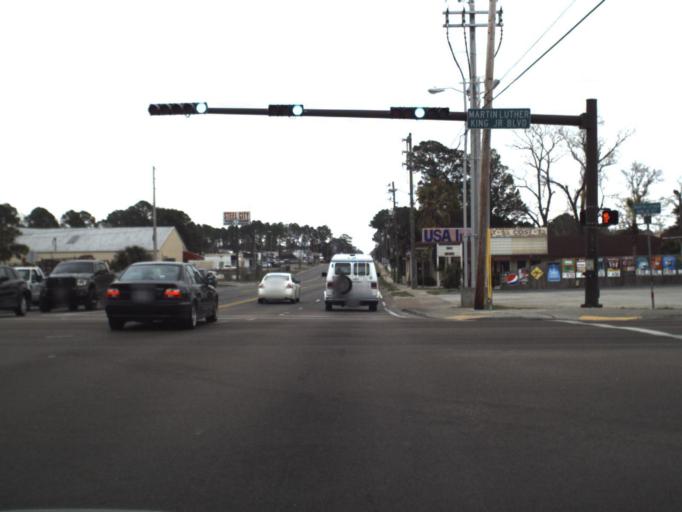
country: US
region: Florida
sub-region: Bay County
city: Panama City
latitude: 30.1750
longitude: -85.6503
